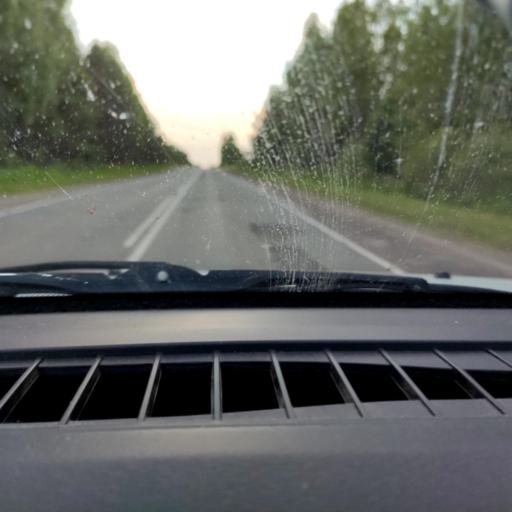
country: RU
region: Perm
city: Kungur
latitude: 57.3498
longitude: 56.7979
